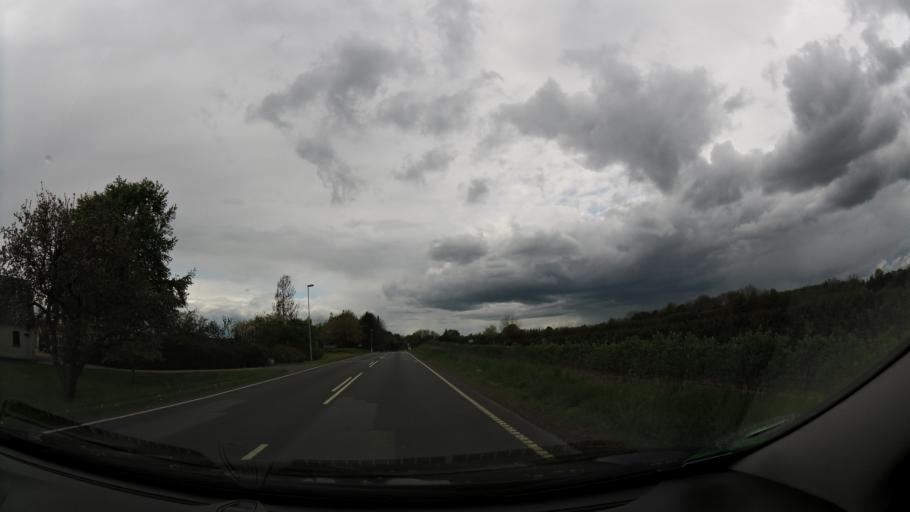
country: DK
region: South Denmark
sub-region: Svendborg Kommune
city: Thuro By
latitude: 55.1617
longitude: 10.7369
